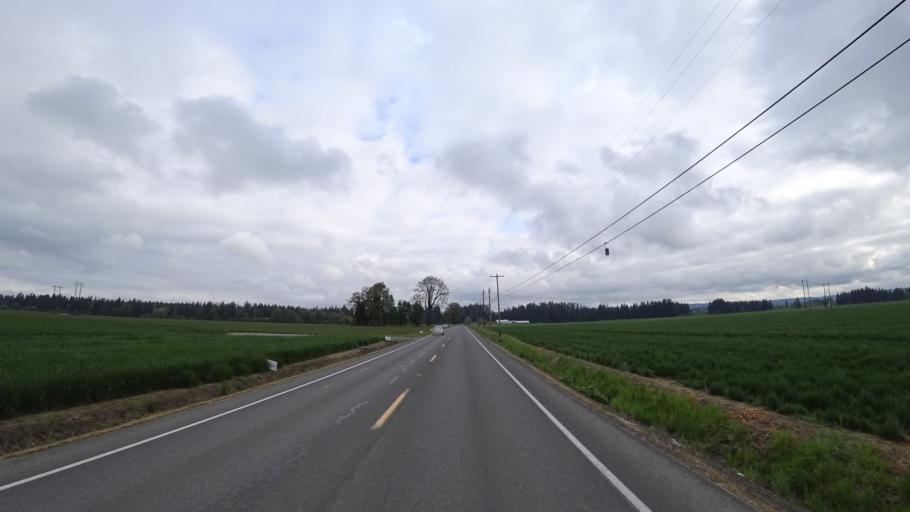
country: US
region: Oregon
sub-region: Washington County
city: Hillsboro
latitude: 45.5555
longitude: -122.9732
